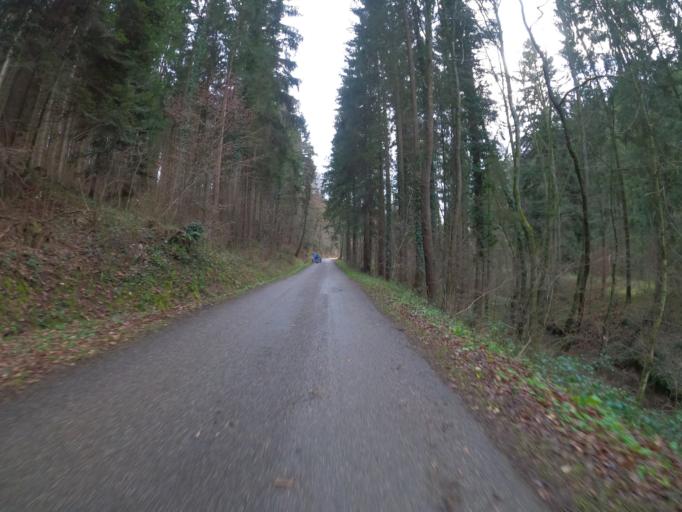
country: DE
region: Baden-Wuerttemberg
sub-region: Regierungsbezirk Stuttgart
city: Lorch
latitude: 48.7828
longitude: 9.7223
